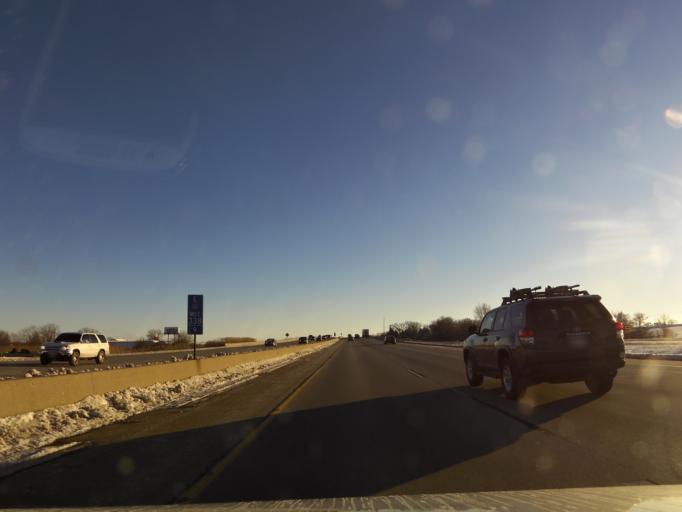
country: US
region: Wisconsin
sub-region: Kenosha County
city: Somers
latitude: 42.6442
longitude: -87.9528
